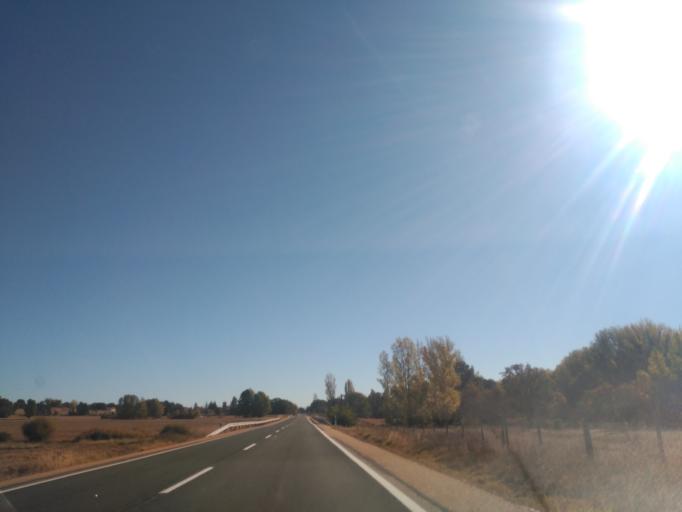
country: ES
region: Castille and Leon
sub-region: Provincia de Soria
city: Cidones
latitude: 41.8132
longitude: -2.6511
